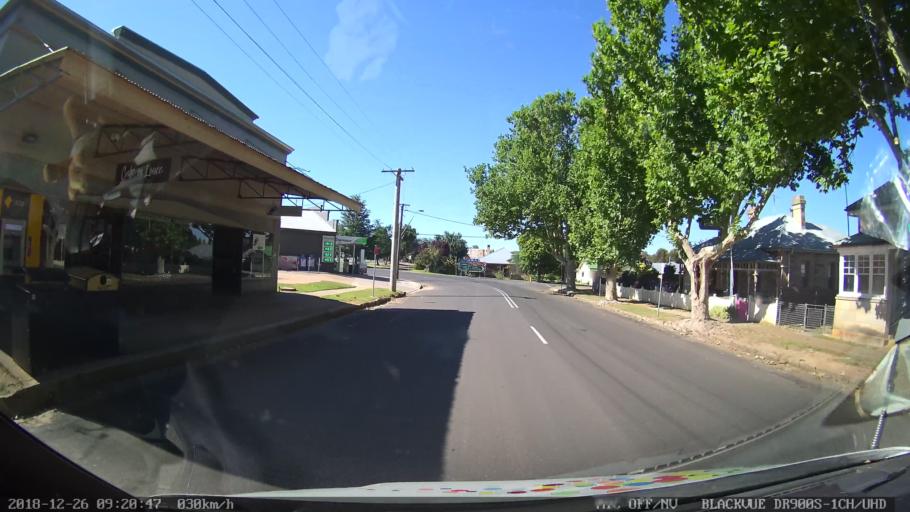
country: AU
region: New South Wales
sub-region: Mid-Western Regional
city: Kandos
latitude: -32.7981
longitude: 149.9711
